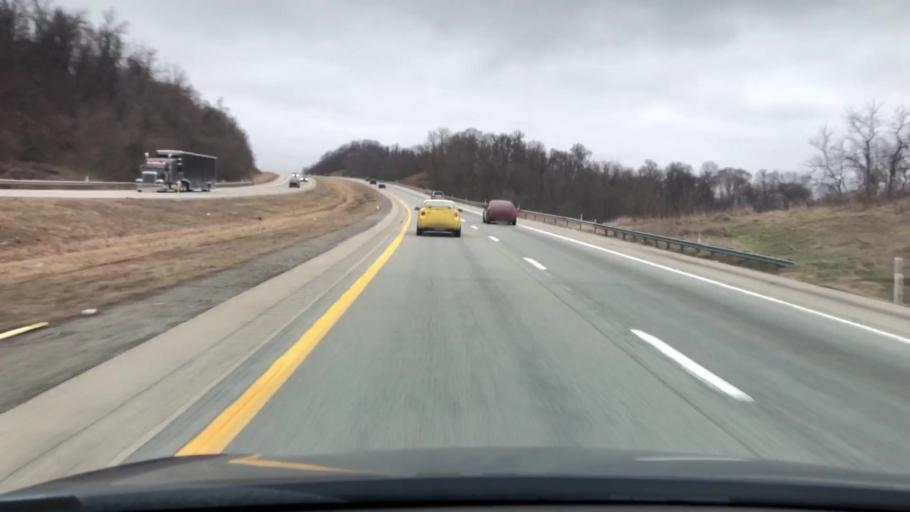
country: US
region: Pennsylvania
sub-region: Greene County
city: Morrisville
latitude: 39.8380
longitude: -80.1122
